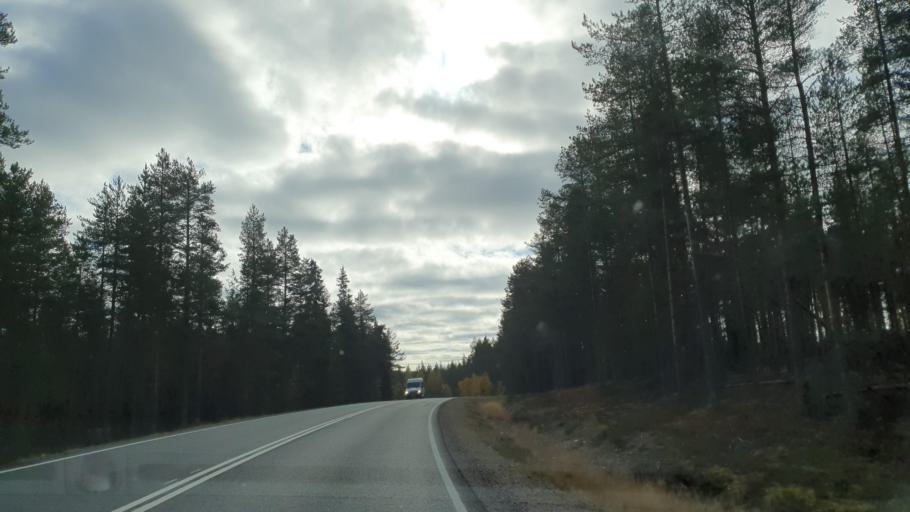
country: FI
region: Northern Ostrobothnia
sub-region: Oulunkaari
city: Pudasjaervi
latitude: 65.3489
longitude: 27.3943
